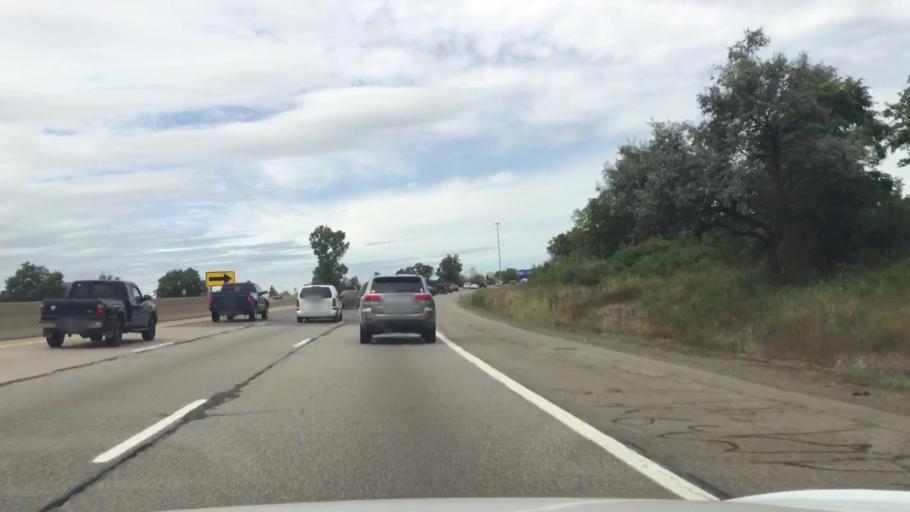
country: US
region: Michigan
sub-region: Oakland County
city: Auburn Hills
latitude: 42.6961
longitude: -83.2677
